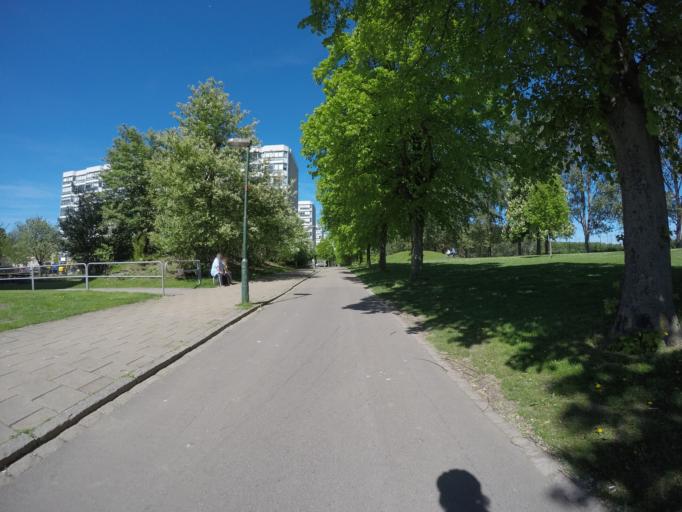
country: SE
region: Skane
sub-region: Burlovs Kommun
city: Arloev
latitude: 55.5884
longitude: 13.0497
